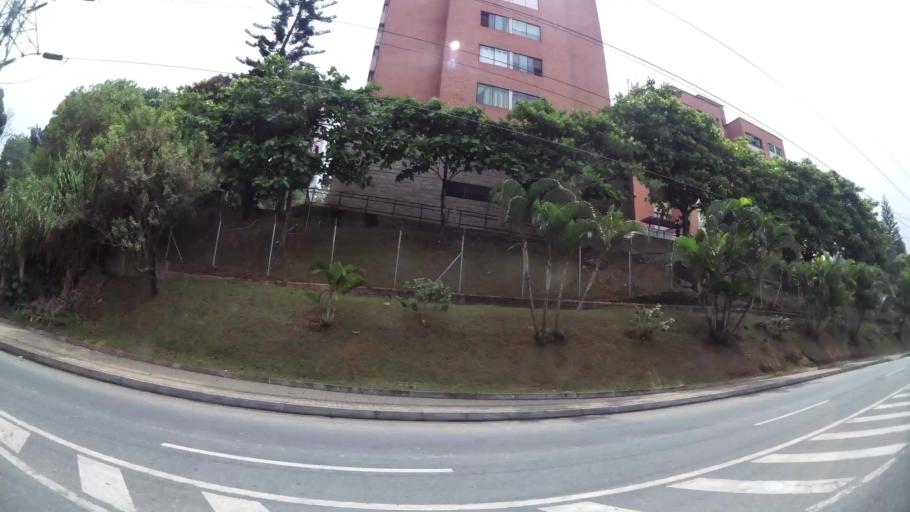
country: CO
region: Antioquia
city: Medellin
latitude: 6.2301
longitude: -75.5639
